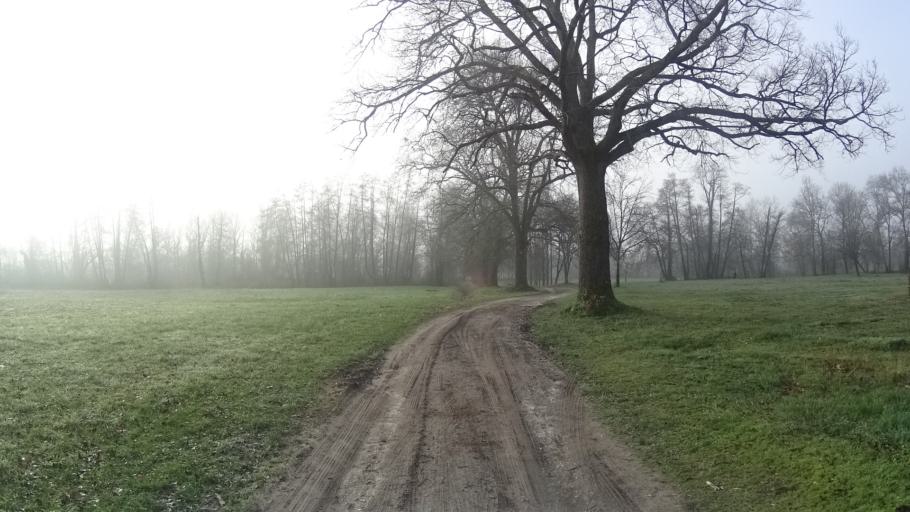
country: FR
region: Poitou-Charentes
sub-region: Departement de la Charente-Maritime
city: Saint-Aigulin
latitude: 45.1504
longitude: -0.0140
